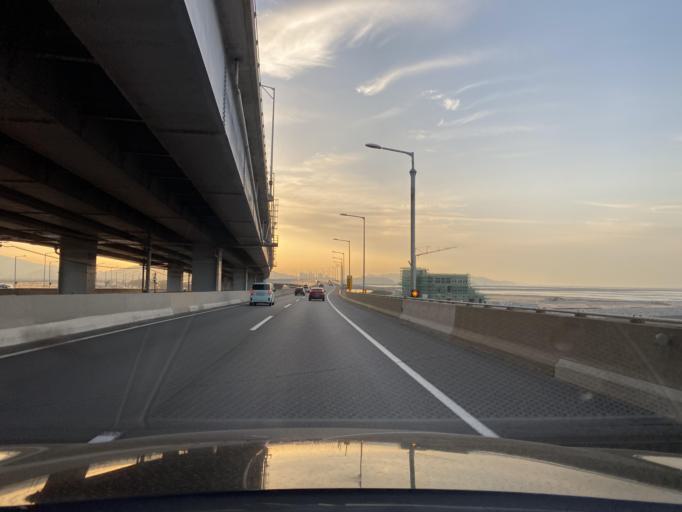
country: KR
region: Gyeonggi-do
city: Tongjin
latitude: 37.5414
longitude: 126.5710
